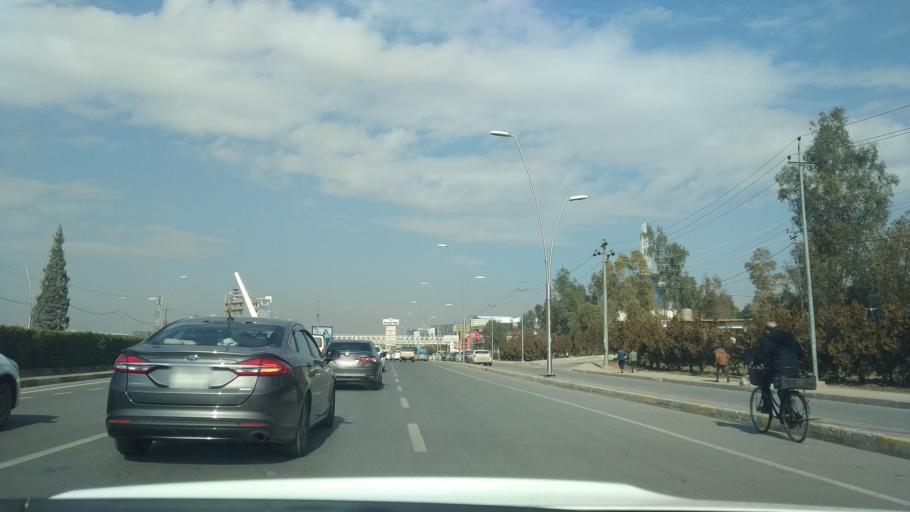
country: IQ
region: Arbil
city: Erbil
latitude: 36.2068
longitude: 44.0448
